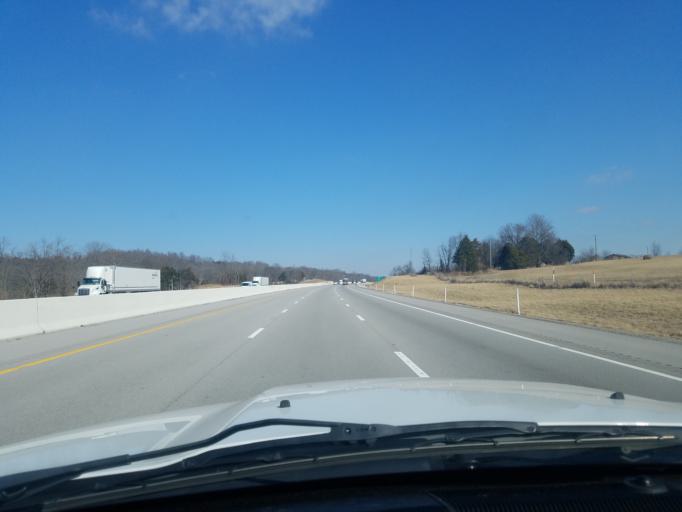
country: US
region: Kentucky
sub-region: Hart County
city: Munfordville
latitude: 37.2601
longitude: -85.9227
